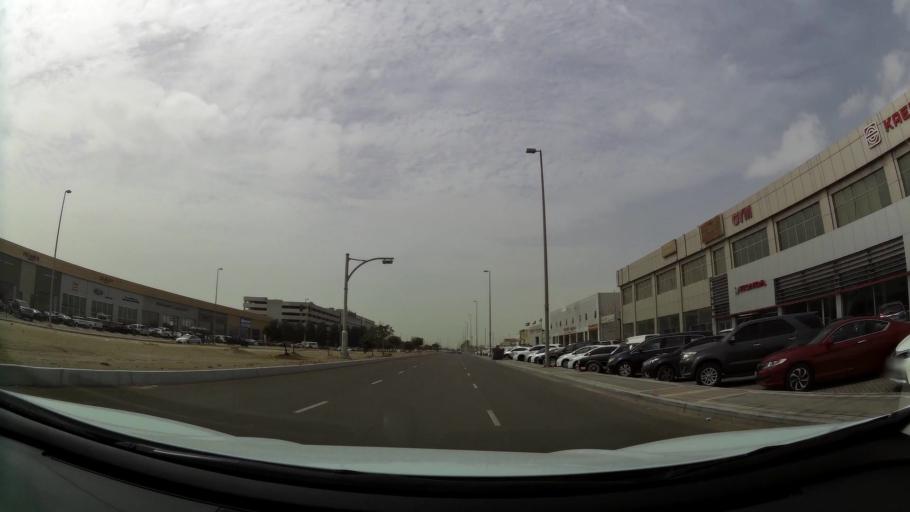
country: AE
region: Abu Dhabi
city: Abu Dhabi
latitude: 24.3692
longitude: 54.5209
